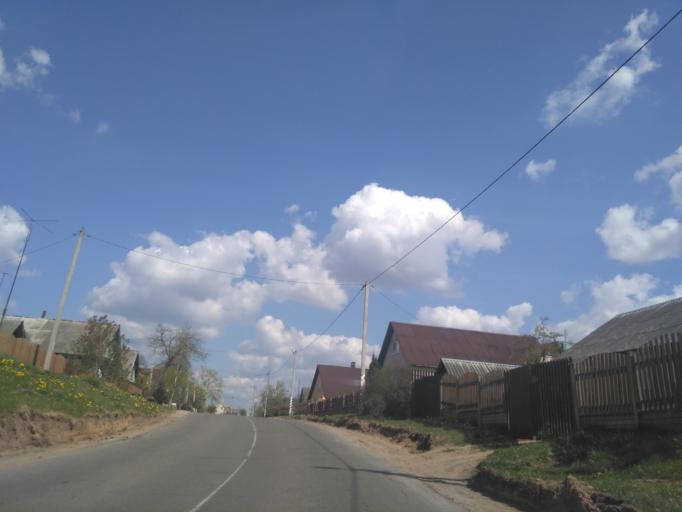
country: BY
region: Minsk
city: Radashkovichy
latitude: 54.1614
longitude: 27.2448
